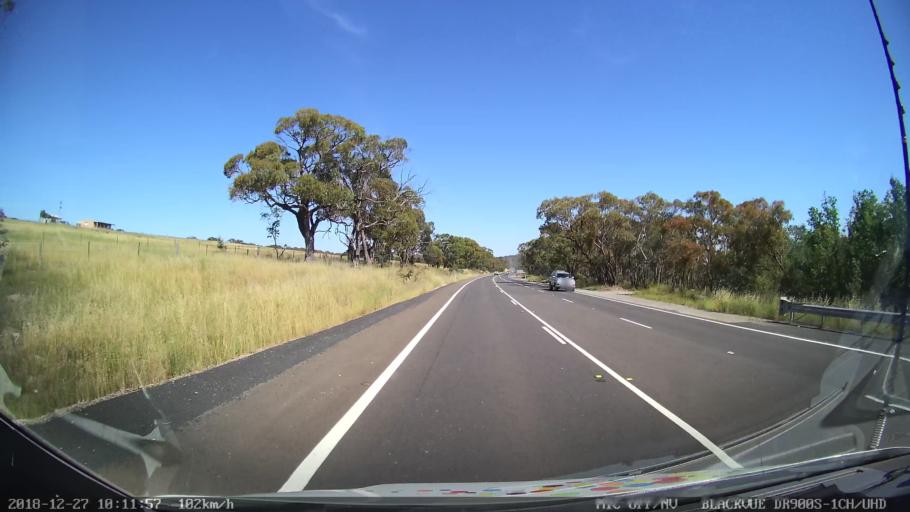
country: AU
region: New South Wales
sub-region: Bathurst Regional
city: Kelso
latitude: -33.4484
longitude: 149.7664
